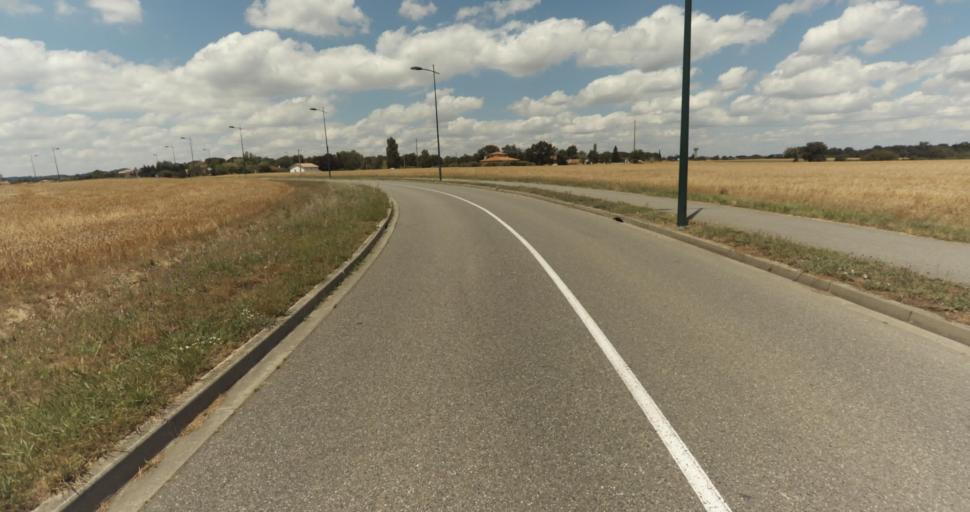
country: FR
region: Midi-Pyrenees
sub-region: Departement de la Haute-Garonne
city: Fontenilles
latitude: 43.5389
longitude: 1.1903
